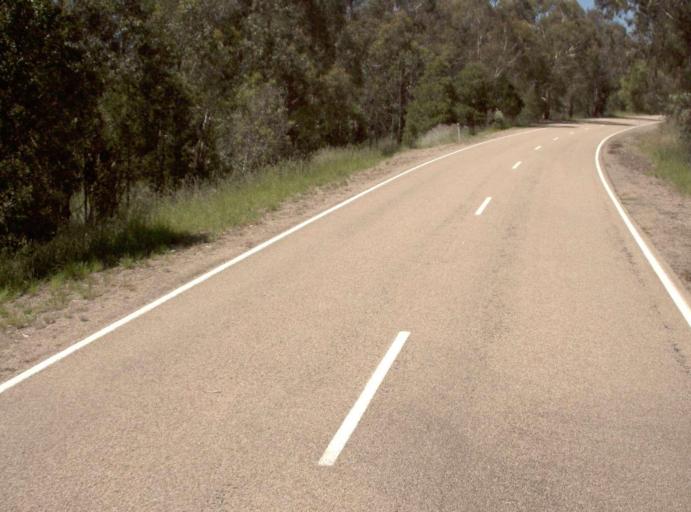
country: AU
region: Victoria
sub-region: East Gippsland
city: Lakes Entrance
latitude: -37.2095
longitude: 148.2696
